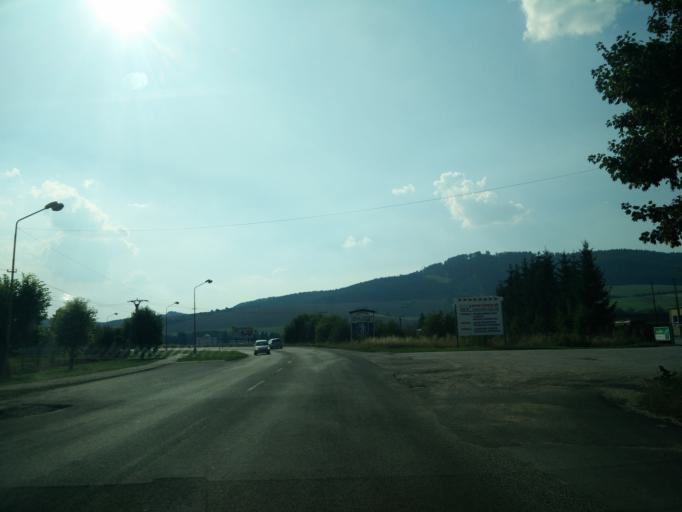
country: SK
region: Zilinsky
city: Rajec
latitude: 49.0954
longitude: 18.6417
